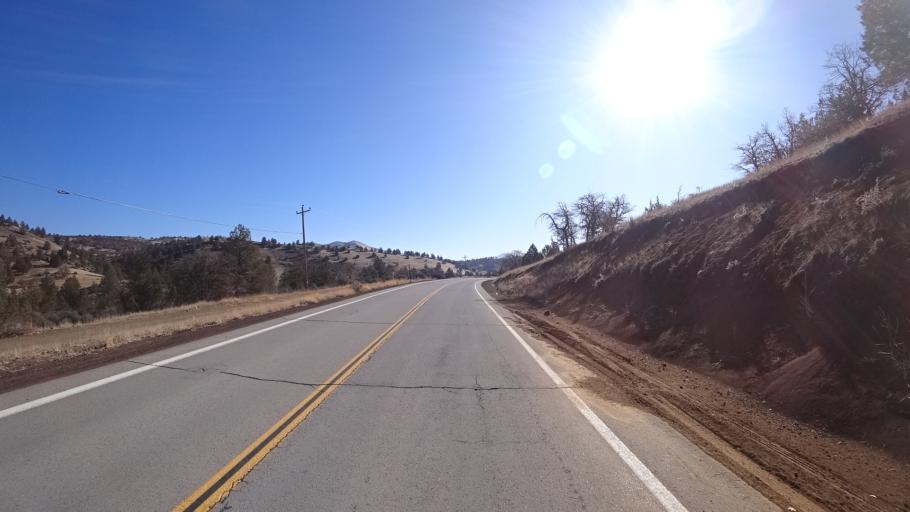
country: US
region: California
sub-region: Siskiyou County
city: Montague
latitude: 41.8726
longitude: -122.4746
